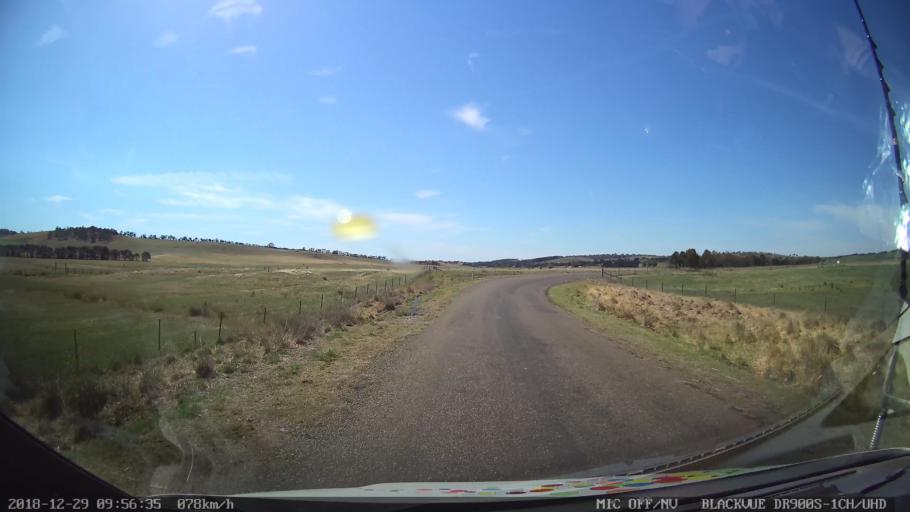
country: AU
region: New South Wales
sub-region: Goulburn Mulwaree
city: Goulburn
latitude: -34.7780
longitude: 149.4813
